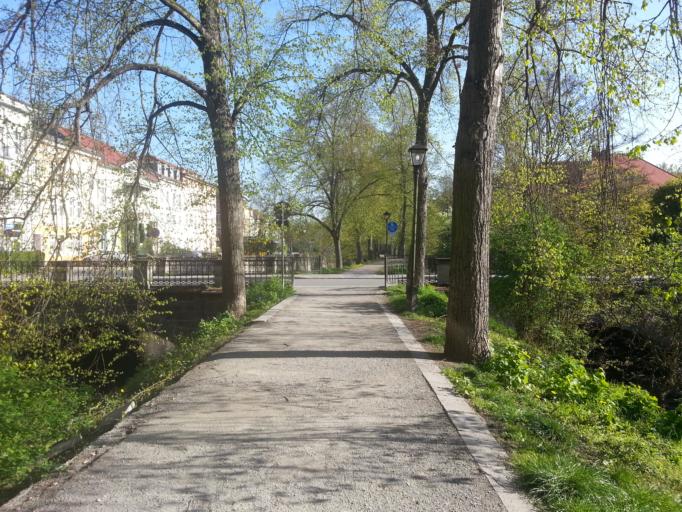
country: DE
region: Thuringia
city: Meiningen
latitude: 50.5666
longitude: 10.4173
